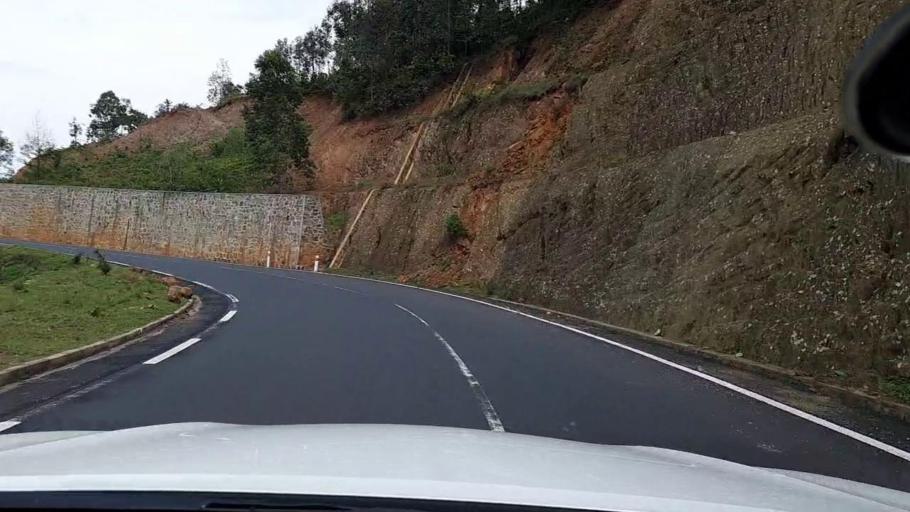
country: RW
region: Western Province
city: Kibuye
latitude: -2.1815
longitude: 29.2901
